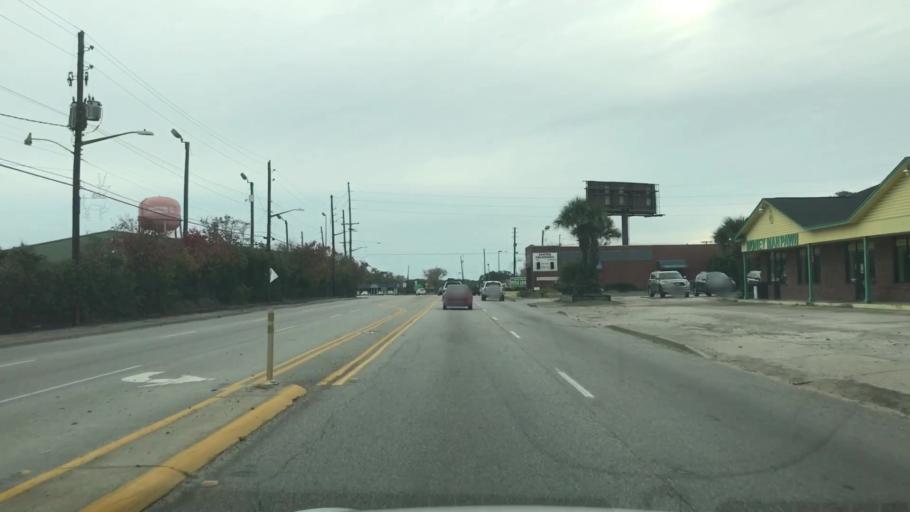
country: US
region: South Carolina
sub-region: Georgetown County
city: Georgetown
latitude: 33.3663
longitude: -79.2942
